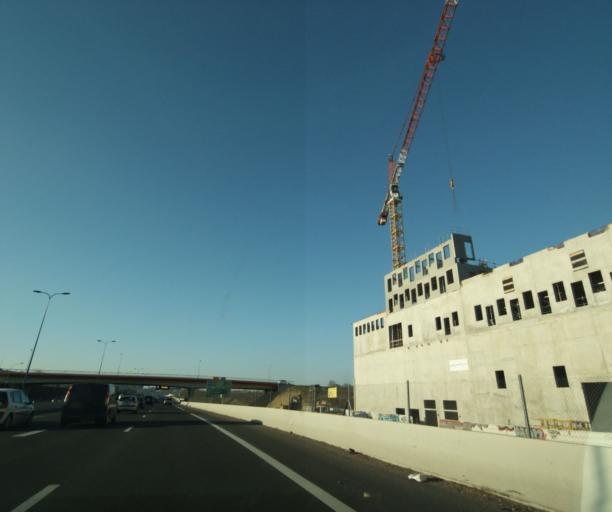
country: FR
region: Midi-Pyrenees
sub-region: Departement de la Haute-Garonne
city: Ramonville-Saint-Agne
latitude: 43.5627
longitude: 1.4881
